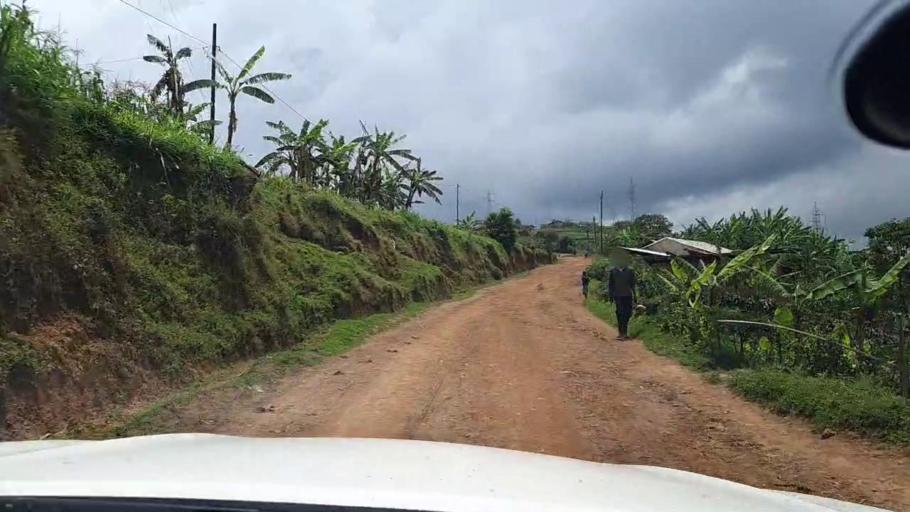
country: RW
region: Western Province
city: Kibuye
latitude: -2.1695
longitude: 29.4315
